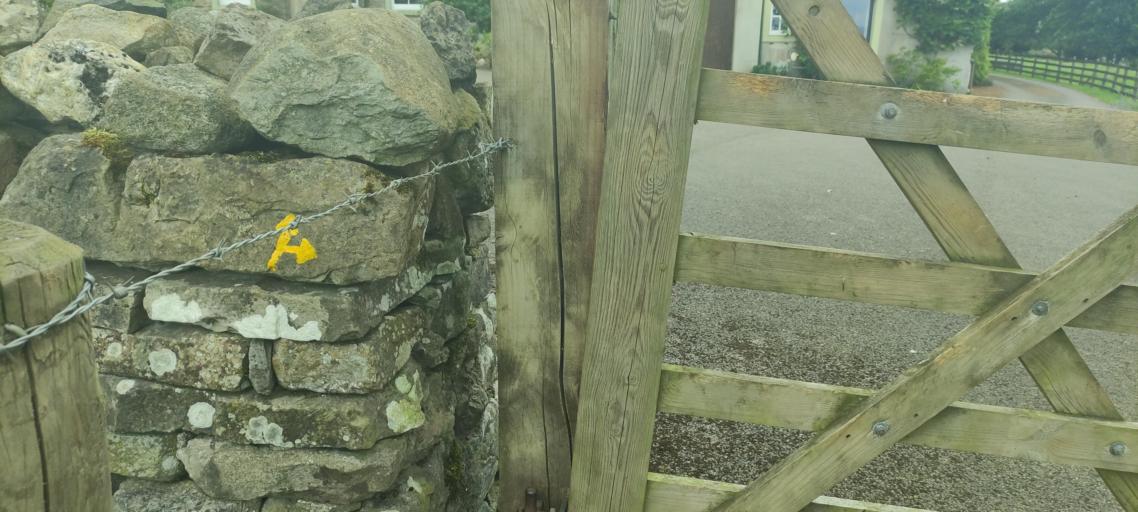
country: GB
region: England
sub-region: Cumbria
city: Wigton
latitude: 54.7419
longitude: -3.0415
